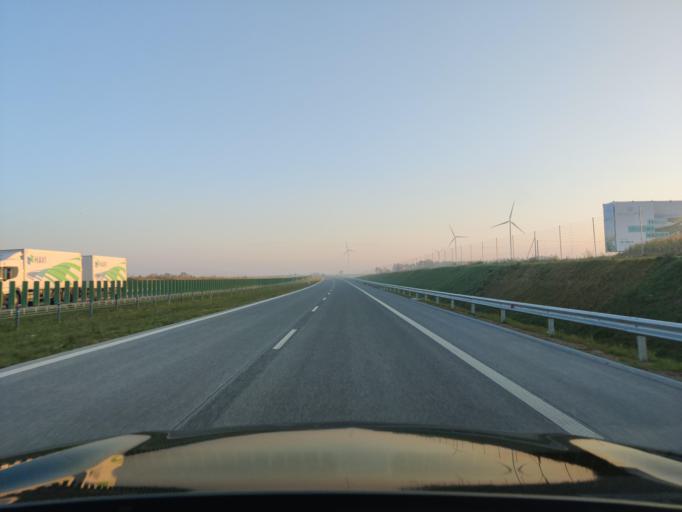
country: PL
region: Masovian Voivodeship
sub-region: Powiat mlawski
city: Wisniewo
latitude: 53.0380
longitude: 20.3559
